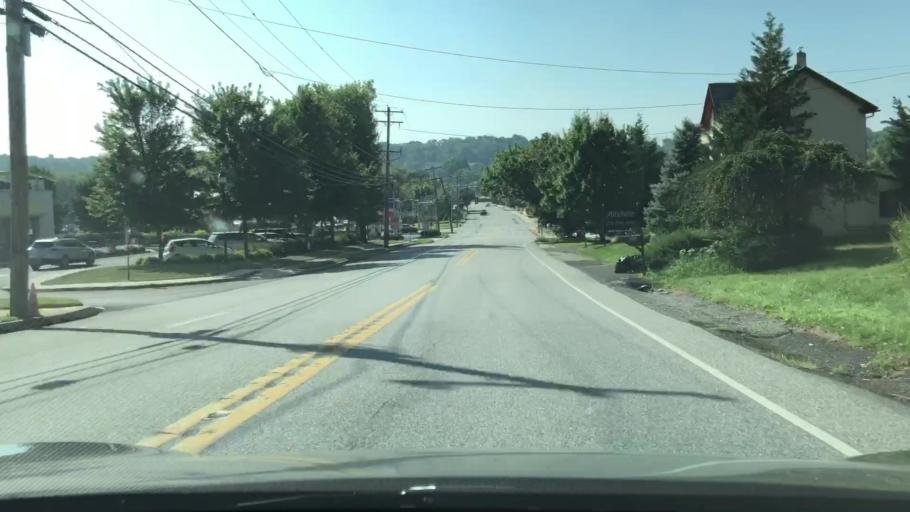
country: US
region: Pennsylvania
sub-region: Montgomery County
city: Dresher
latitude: 40.1444
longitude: -75.1684
